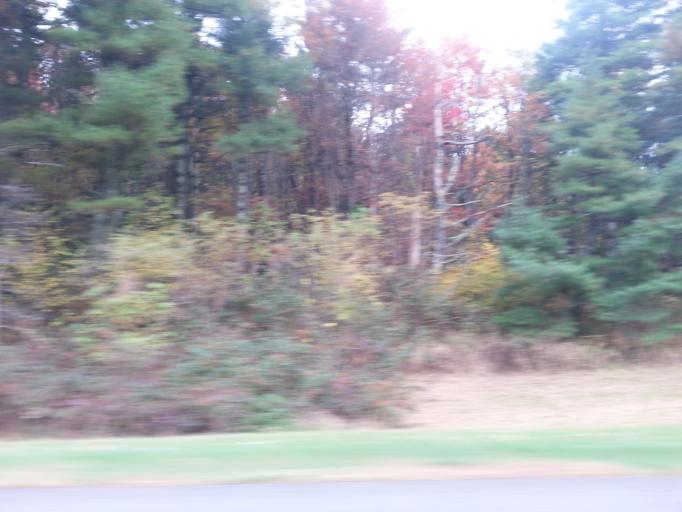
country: US
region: North Carolina
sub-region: Wilkes County
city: Millers Creek
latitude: 36.2841
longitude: -81.3733
